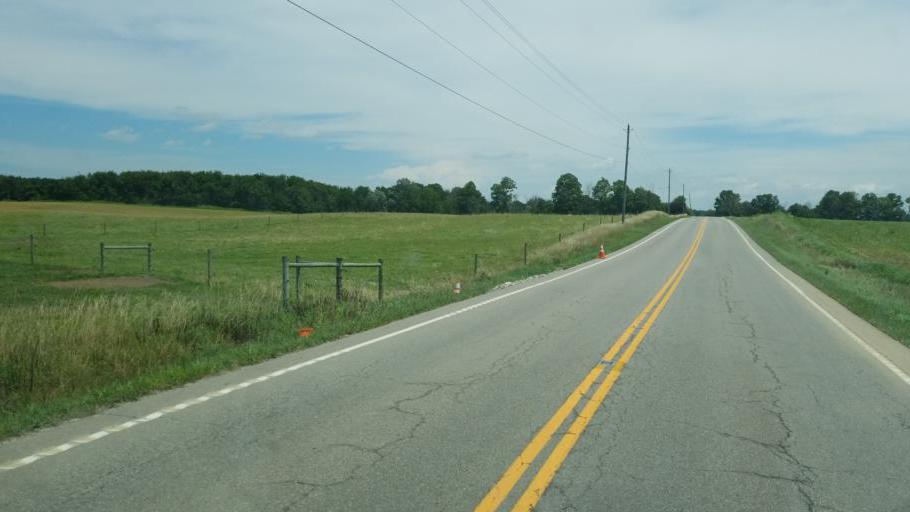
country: US
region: Ohio
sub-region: Richland County
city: Lincoln Heights
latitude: 40.8874
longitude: -82.5291
